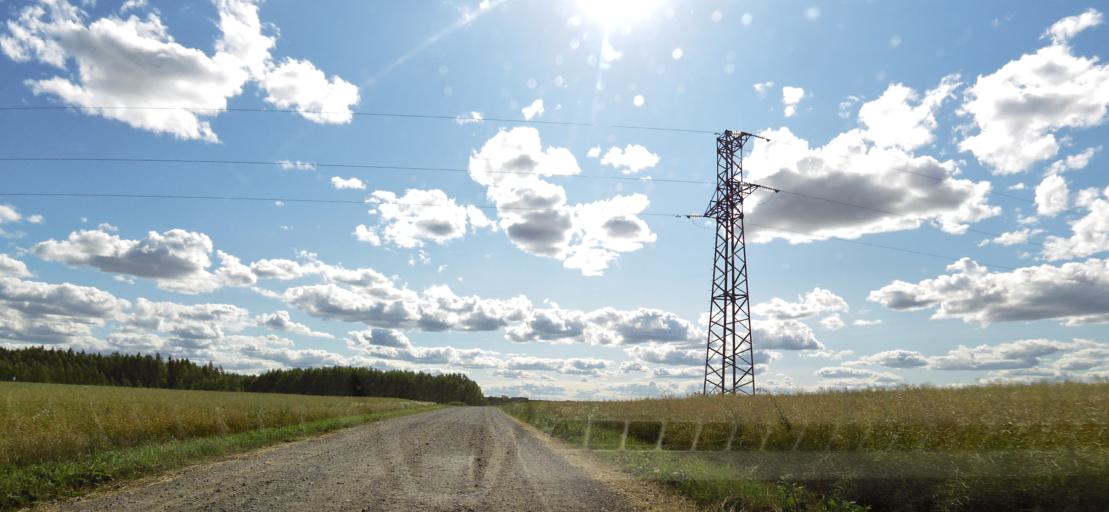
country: LT
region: Panevezys
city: Pasvalys
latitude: 56.1269
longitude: 24.3182
